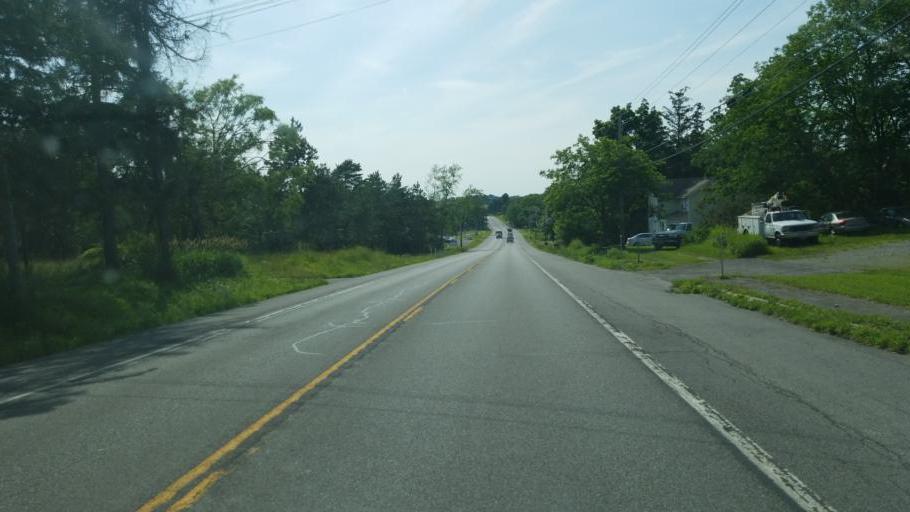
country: US
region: New York
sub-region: Ontario County
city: Holcomb
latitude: 42.9014
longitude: -77.4639
